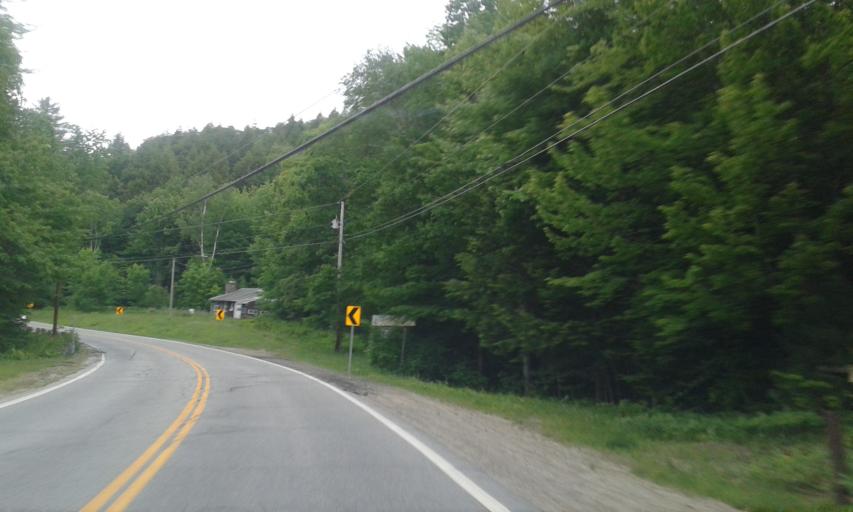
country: US
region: New Hampshire
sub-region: Grafton County
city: Woodstock
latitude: 43.9924
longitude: -71.6860
